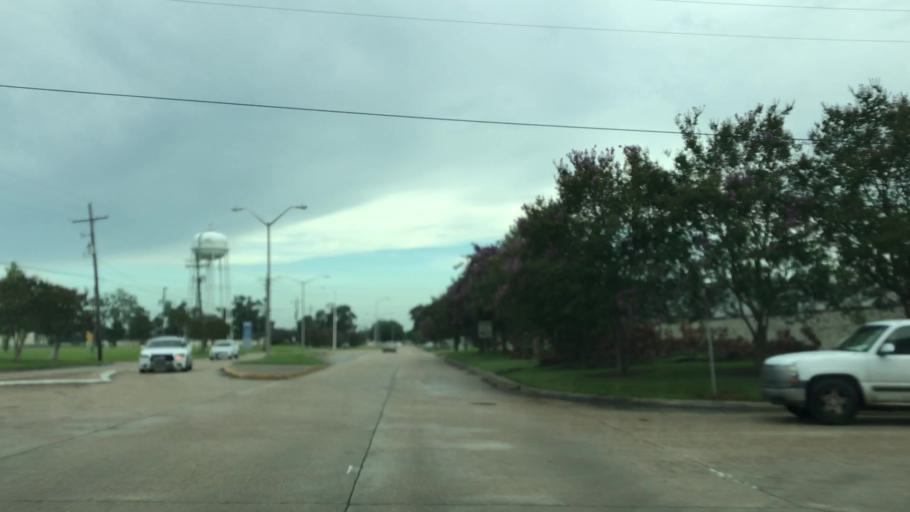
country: US
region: Louisiana
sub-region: East Baton Rouge Parish
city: Brownsfield
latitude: 30.5332
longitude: -91.1614
